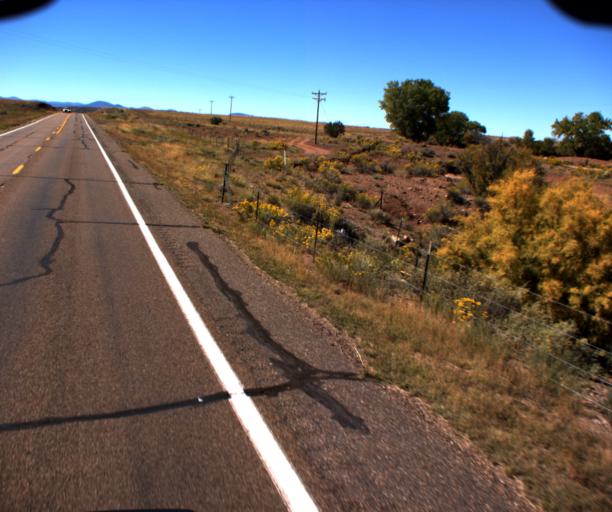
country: US
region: Arizona
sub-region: Apache County
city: Saint Johns
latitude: 34.4646
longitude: -109.3975
